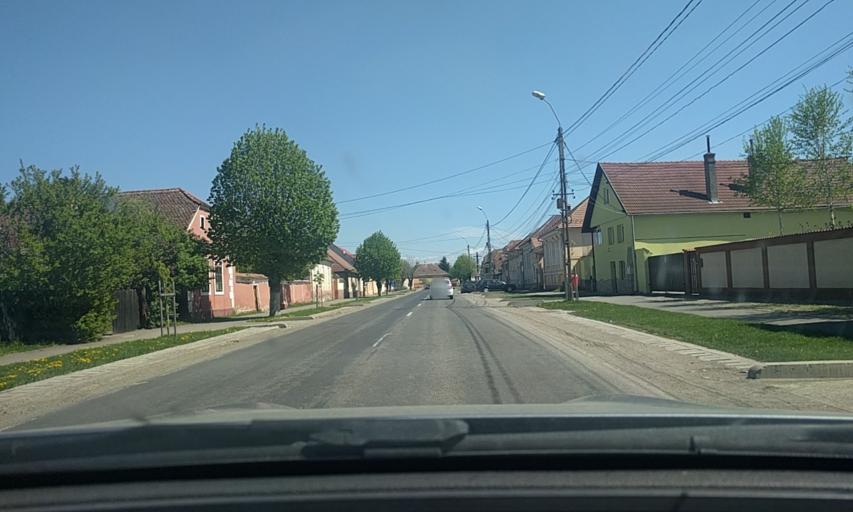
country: RO
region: Brasov
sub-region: Comuna Prejmer
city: Prejmer
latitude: 45.7188
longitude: 25.7750
